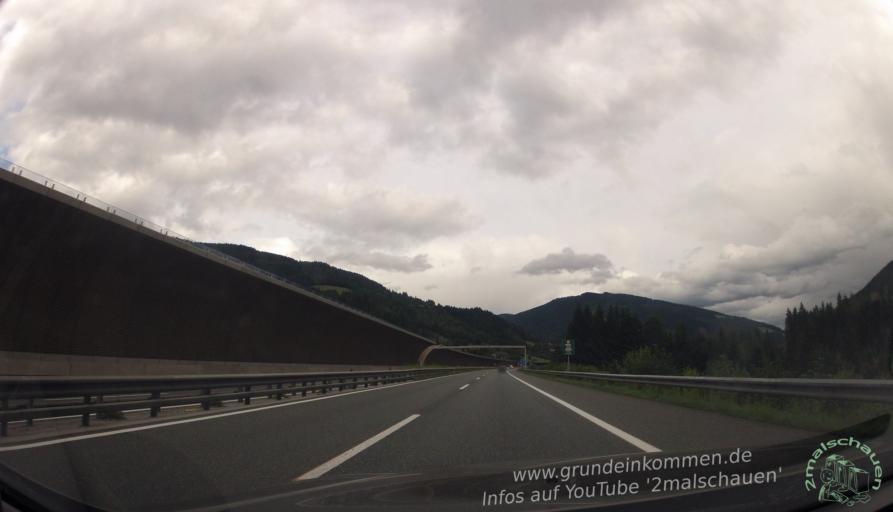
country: AT
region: Salzburg
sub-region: Politischer Bezirk Sankt Johann im Pongau
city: Eben im Pongau
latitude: 47.4227
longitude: 13.3734
